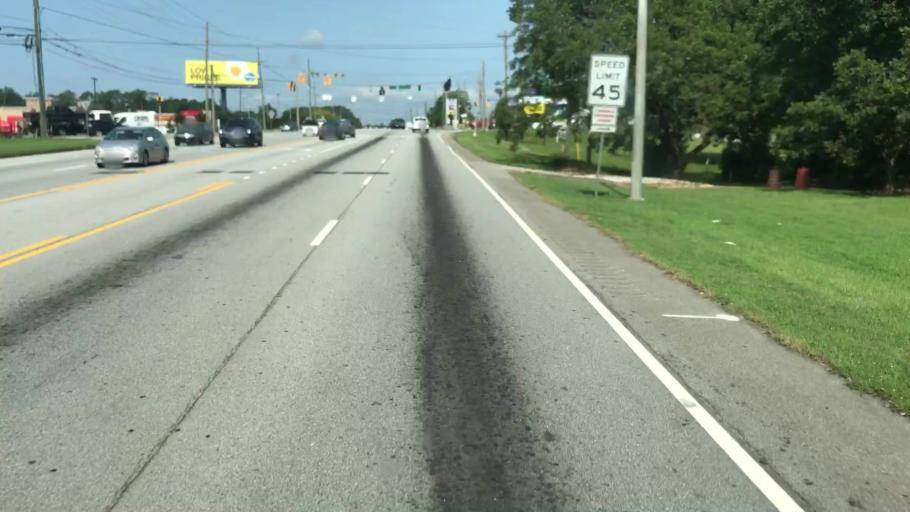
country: US
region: Georgia
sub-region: Walton County
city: Loganville
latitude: 33.8327
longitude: -83.8806
